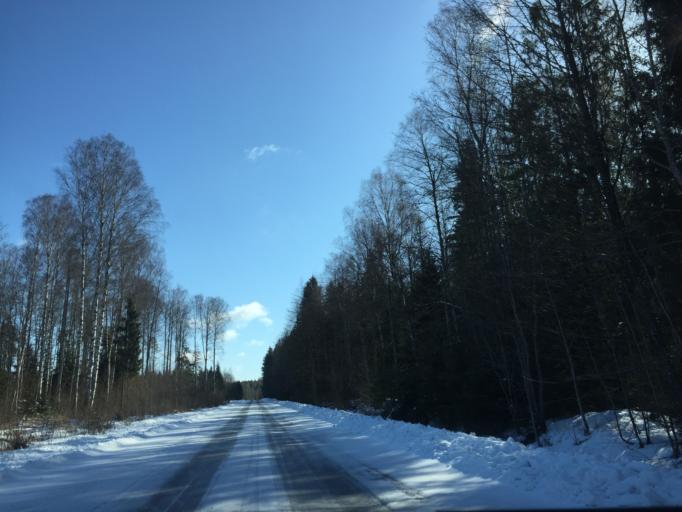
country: LV
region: Salacgrivas
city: Ainazi
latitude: 57.9976
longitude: 24.5537
